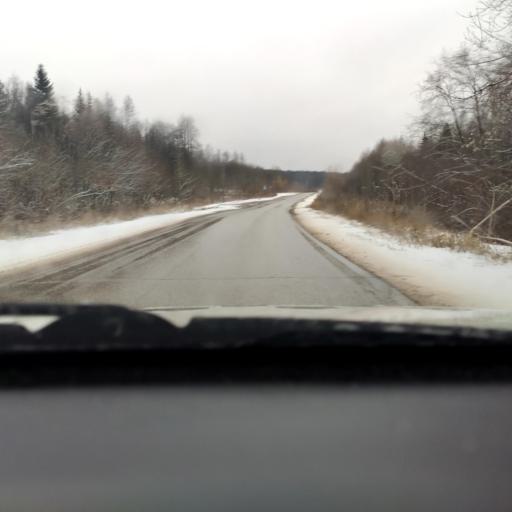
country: RU
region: Perm
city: Ferma
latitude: 57.9787
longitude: 56.3562
